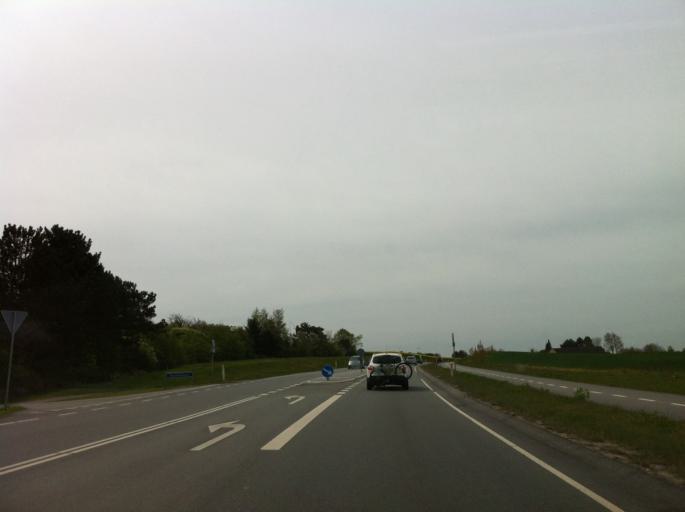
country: DK
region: Capital Region
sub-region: Frederikssund Kommune
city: Slangerup
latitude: 55.8749
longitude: 12.1931
